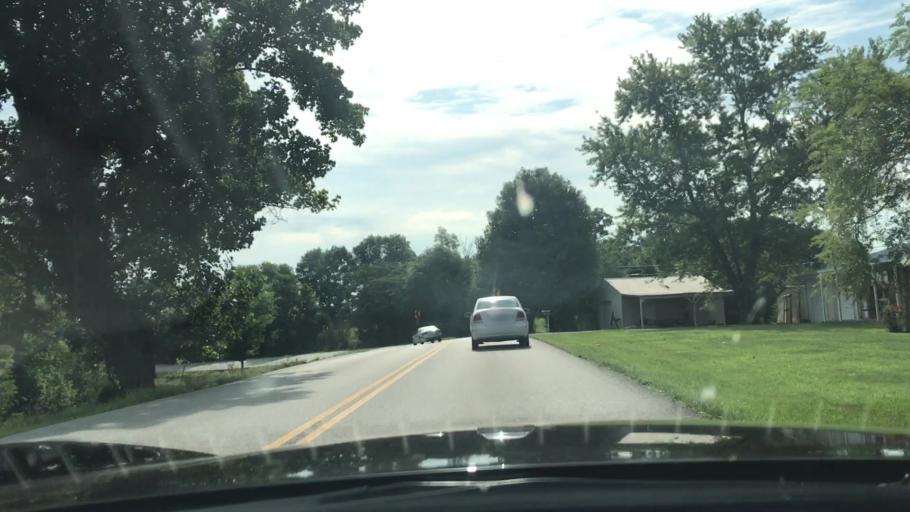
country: US
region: Kentucky
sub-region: Green County
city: Greensburg
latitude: 37.2690
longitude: -85.5341
